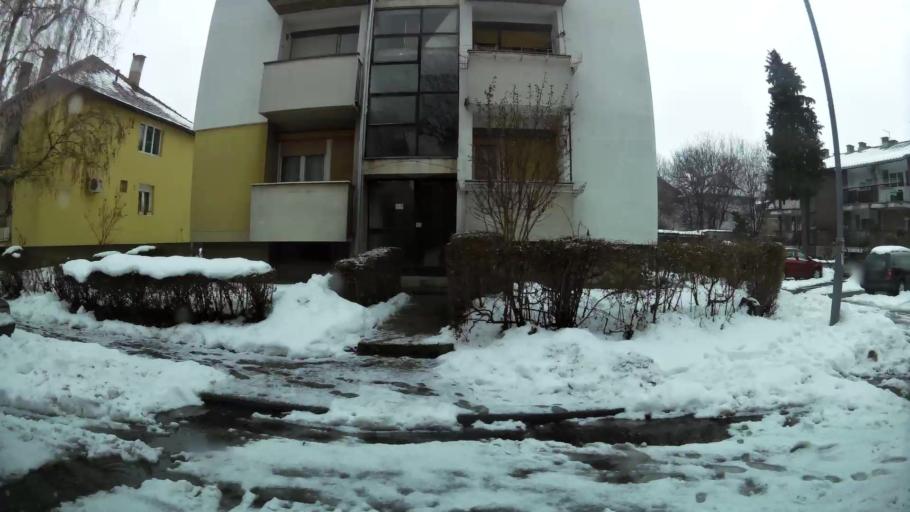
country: RS
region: Central Serbia
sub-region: Belgrade
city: Zemun
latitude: 44.8713
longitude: 20.3211
